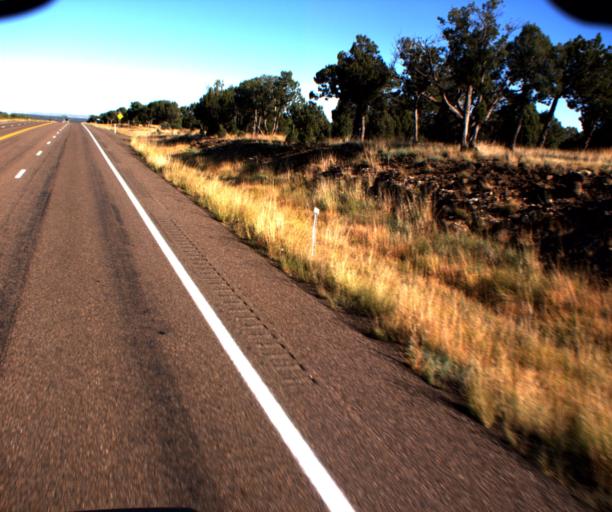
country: US
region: Arizona
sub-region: Navajo County
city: White Mountain Lake
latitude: 34.3338
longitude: -110.0481
